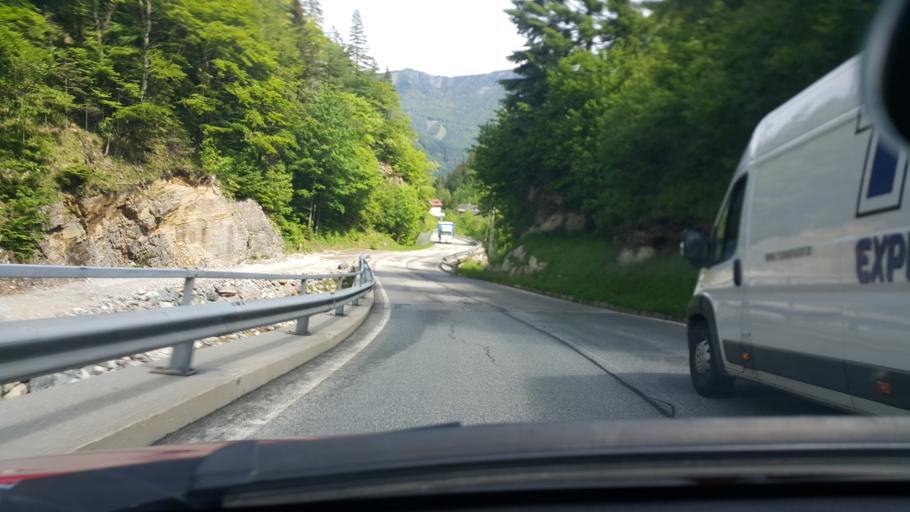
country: AT
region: Carinthia
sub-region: Politischer Bezirk Klagenfurt Land
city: Ferlach
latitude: 46.4573
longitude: 14.2592
